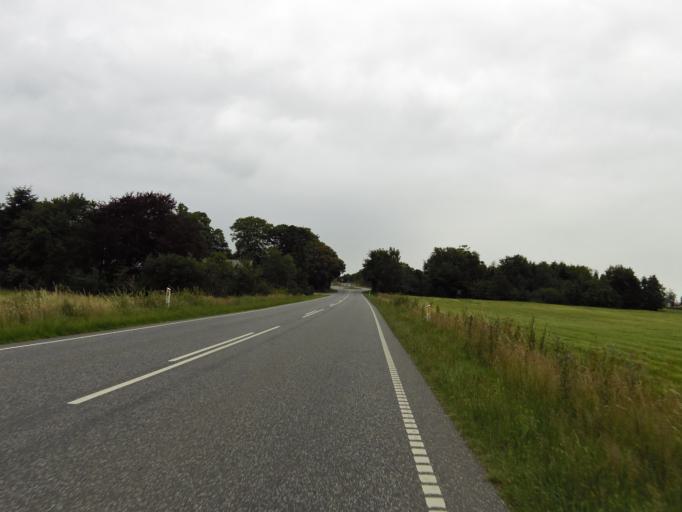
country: DK
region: South Denmark
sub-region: Tonder Kommune
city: Toftlund
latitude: 55.1669
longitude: 8.9643
